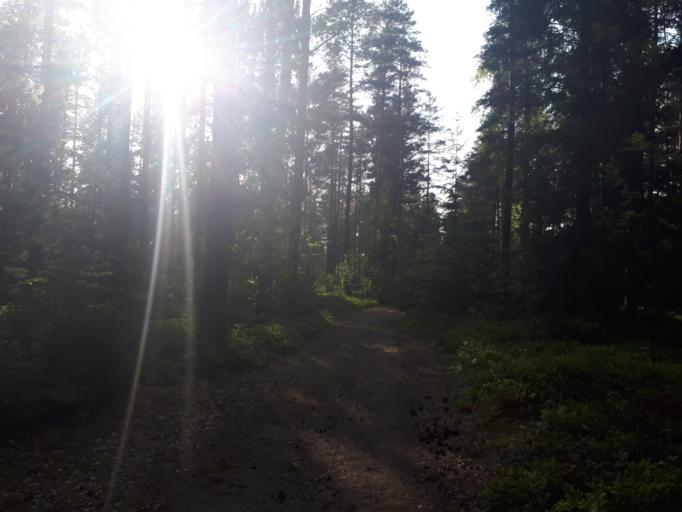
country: SE
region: Soedermanland
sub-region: Flens Kommun
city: Halleforsnas
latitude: 59.0646
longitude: 16.4002
